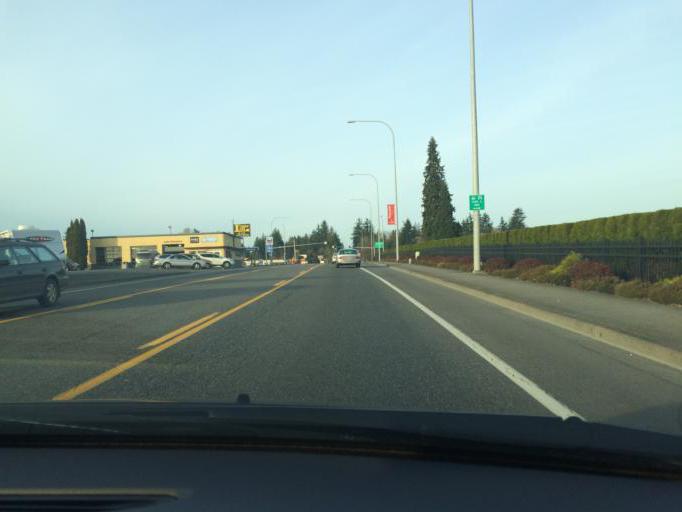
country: US
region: Washington
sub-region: Whatcom County
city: Lynden
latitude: 48.9374
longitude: -122.4854
